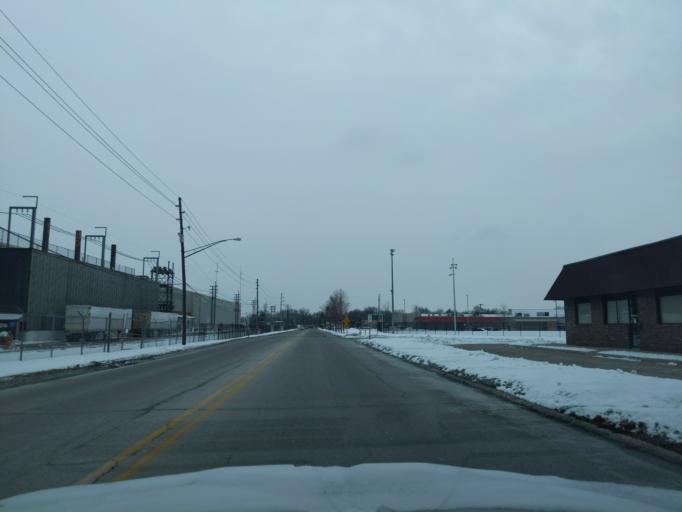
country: US
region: Indiana
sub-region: Tippecanoe County
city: Lafayette
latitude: 40.3996
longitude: -86.8672
